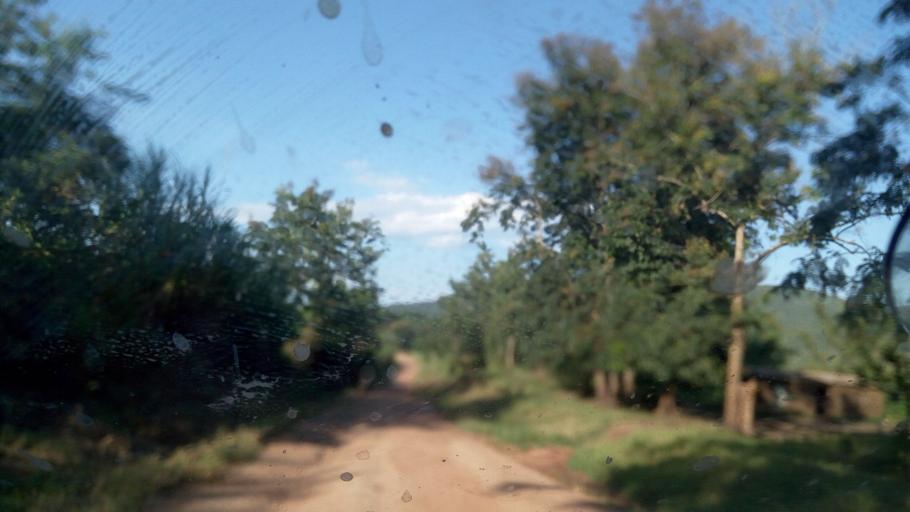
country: BI
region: Bururi
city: Rumonge
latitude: -4.2865
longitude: 28.9600
